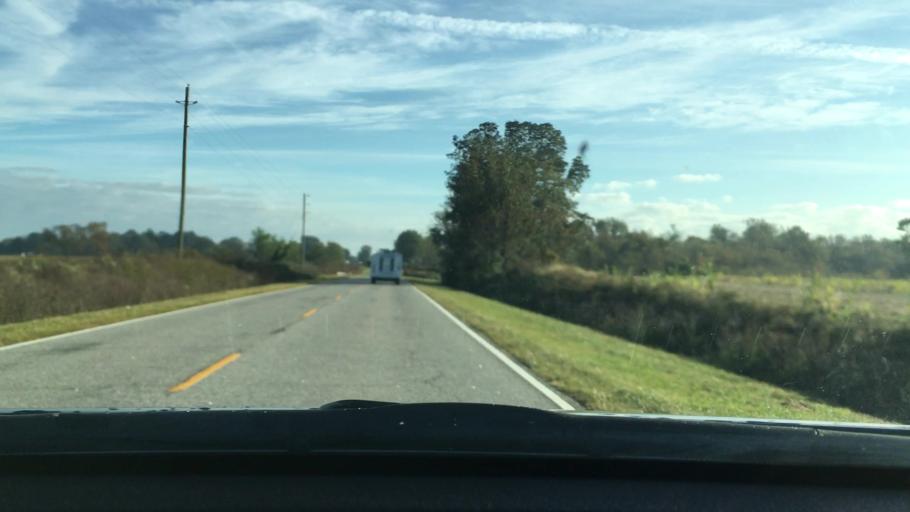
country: US
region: South Carolina
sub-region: Sumter County
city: East Sumter
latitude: 34.0625
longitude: -80.2254
